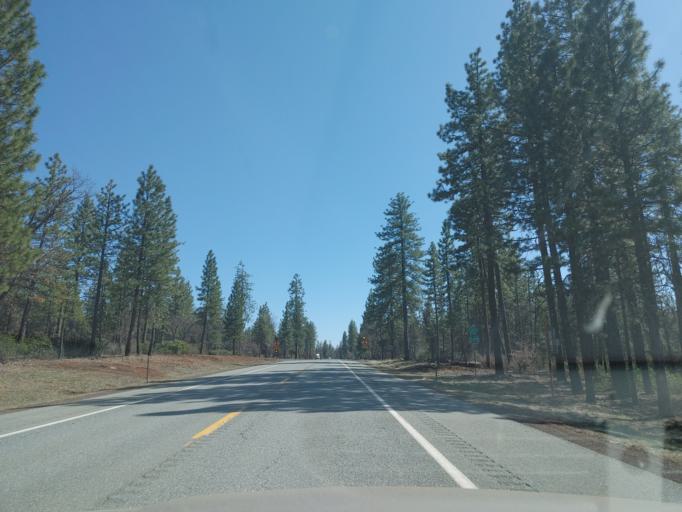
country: US
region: California
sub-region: Shasta County
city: Burney
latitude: 40.9429
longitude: -121.6085
